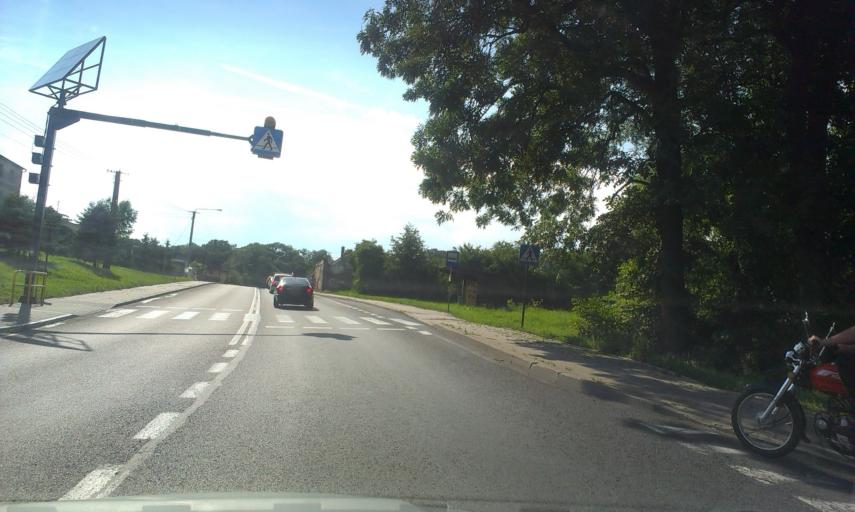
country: PL
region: Kujawsko-Pomorskie
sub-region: Powiat bydgoski
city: Sicienko
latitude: 53.1670
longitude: 17.7767
